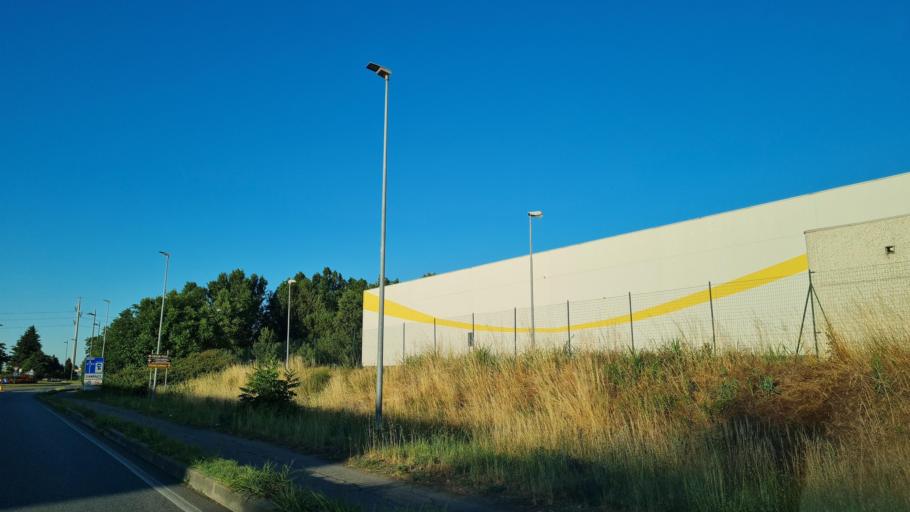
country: IT
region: Piedmont
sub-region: Provincia di Novara
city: Biandrate
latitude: 45.4608
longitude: 8.4643
